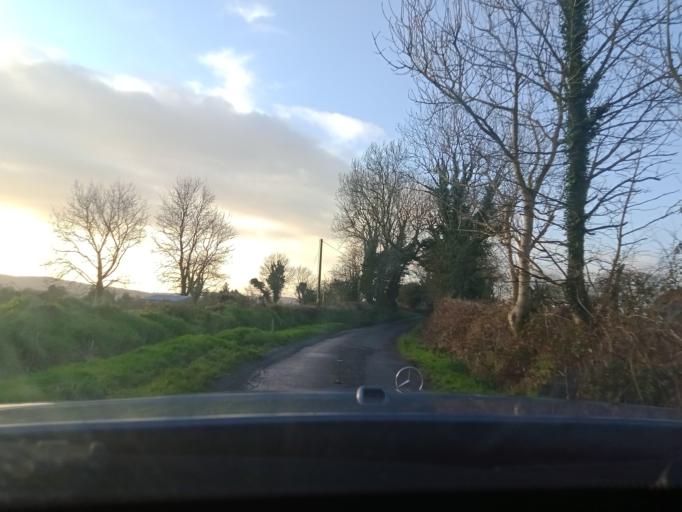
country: IE
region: Leinster
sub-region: Kilkenny
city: Callan
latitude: 52.4597
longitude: -7.4221
